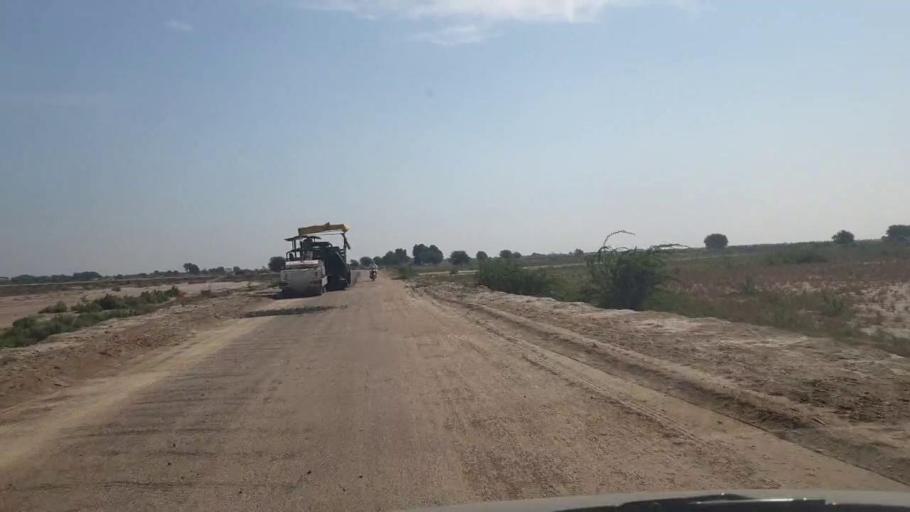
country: PK
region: Sindh
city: Digri
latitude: 24.9734
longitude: 69.1234
